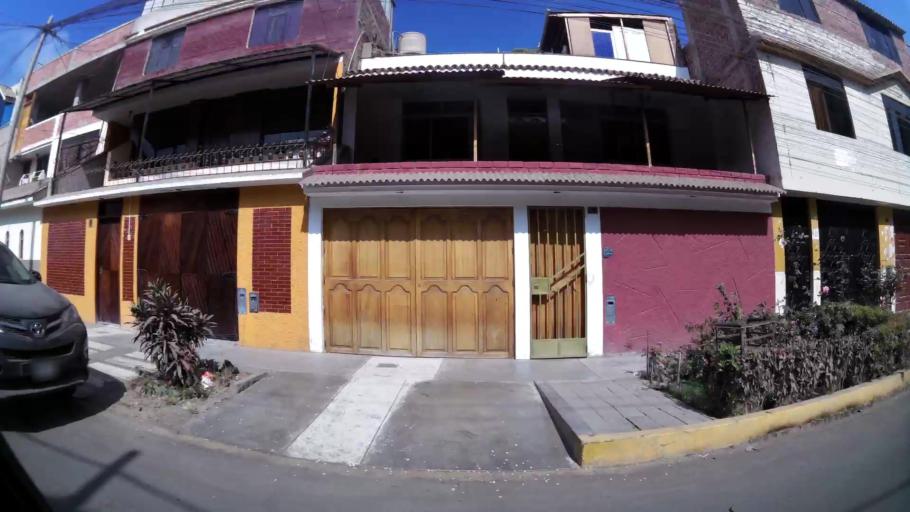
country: PE
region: La Libertad
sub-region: Provincia de Trujillo
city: Trujillo
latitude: -8.1254
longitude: -79.0187
